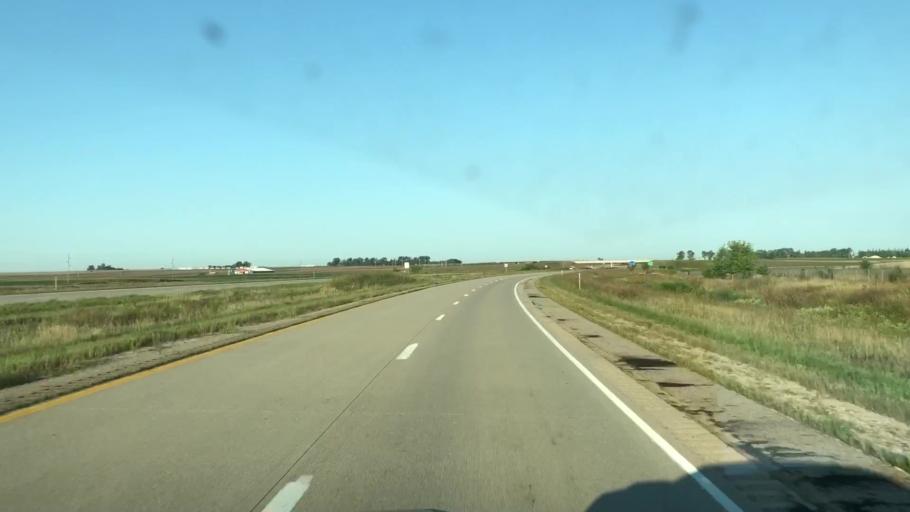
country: US
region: Iowa
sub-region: Osceola County
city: Sibley
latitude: 43.3848
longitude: -95.7298
